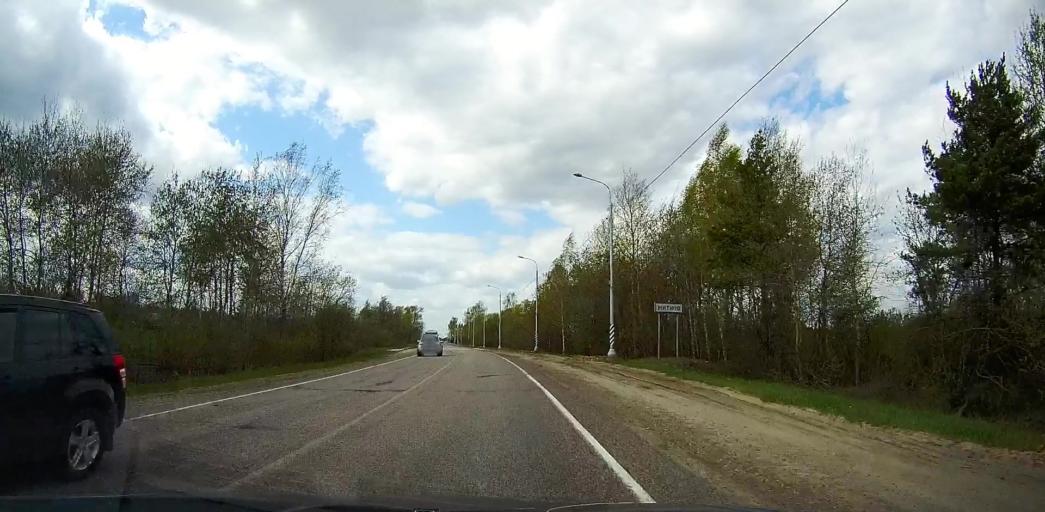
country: RU
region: Moskovskaya
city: Davydovo
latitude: 55.6637
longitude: 38.8042
